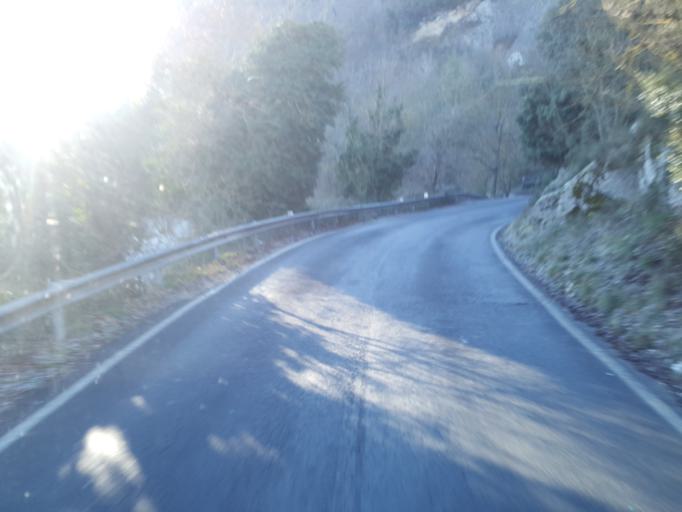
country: IT
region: Umbria
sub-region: Provincia di Terni
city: Arrone
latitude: 42.5428
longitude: 12.7155
